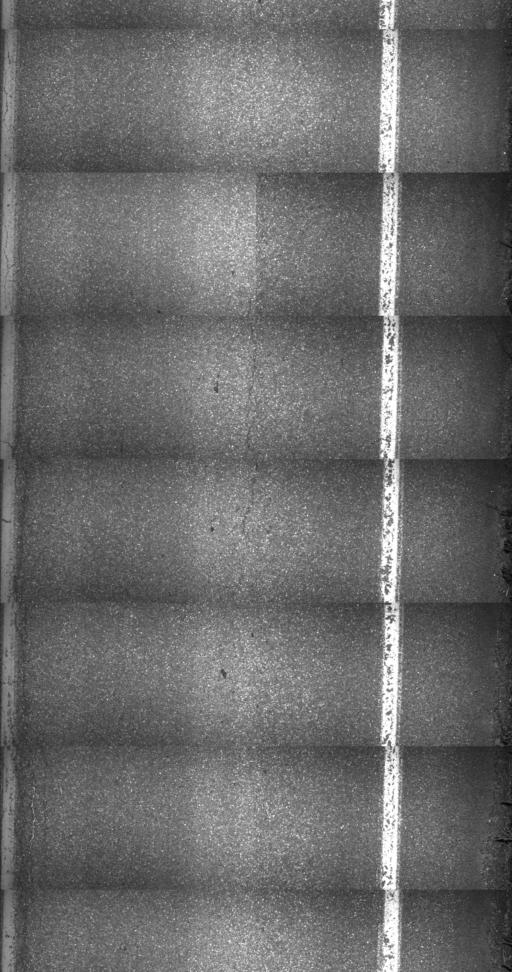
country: US
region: Vermont
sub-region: Franklin County
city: Richford
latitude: 44.9883
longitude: -72.6492
